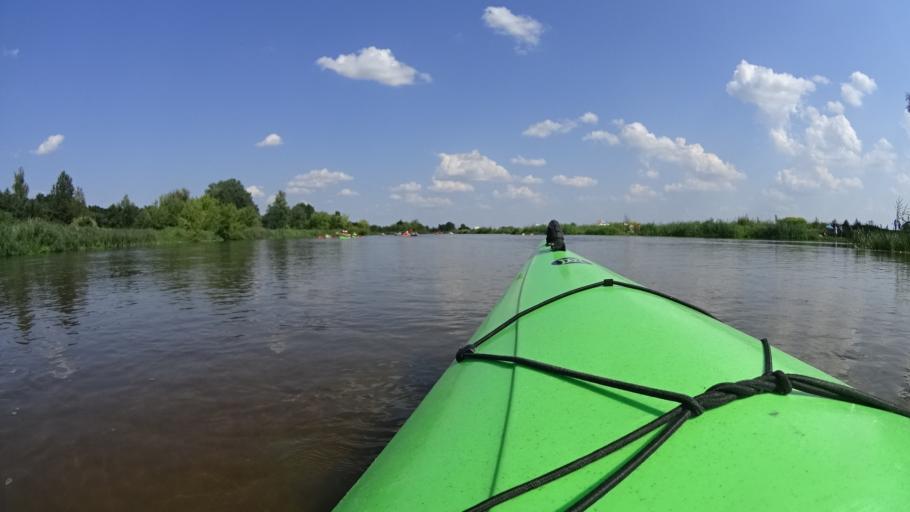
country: PL
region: Masovian Voivodeship
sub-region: Powiat bialobrzeski
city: Wysmierzyce
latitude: 51.6618
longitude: 20.8659
